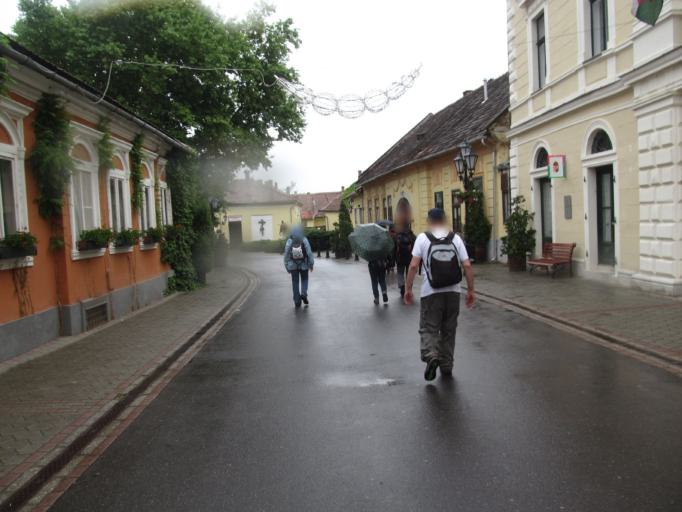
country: HU
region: Borsod-Abauj-Zemplen
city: Tokaj
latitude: 48.1250
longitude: 21.4094
